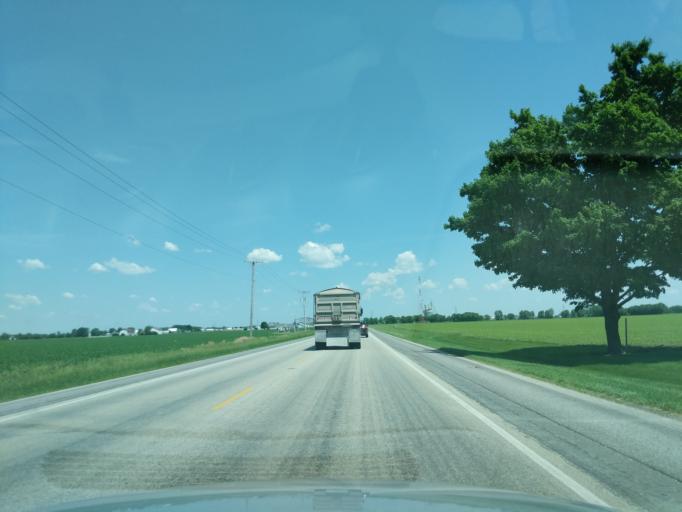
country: US
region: Indiana
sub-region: LaGrange County
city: Topeka
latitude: 41.5267
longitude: -85.5778
